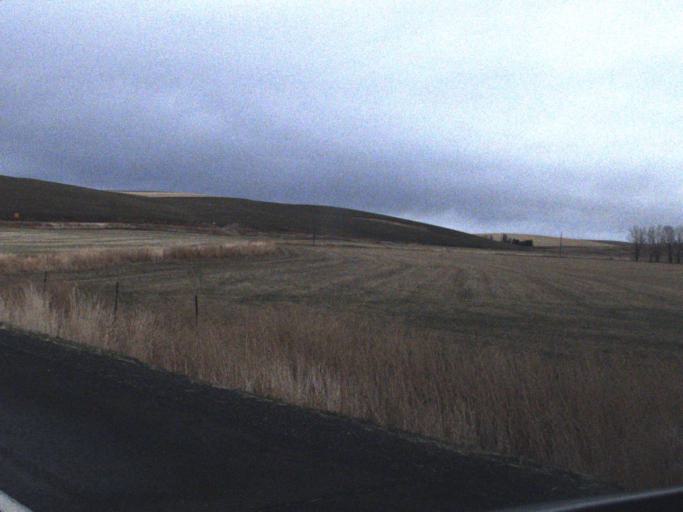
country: US
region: Washington
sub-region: Columbia County
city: Dayton
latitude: 46.3809
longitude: -117.9392
